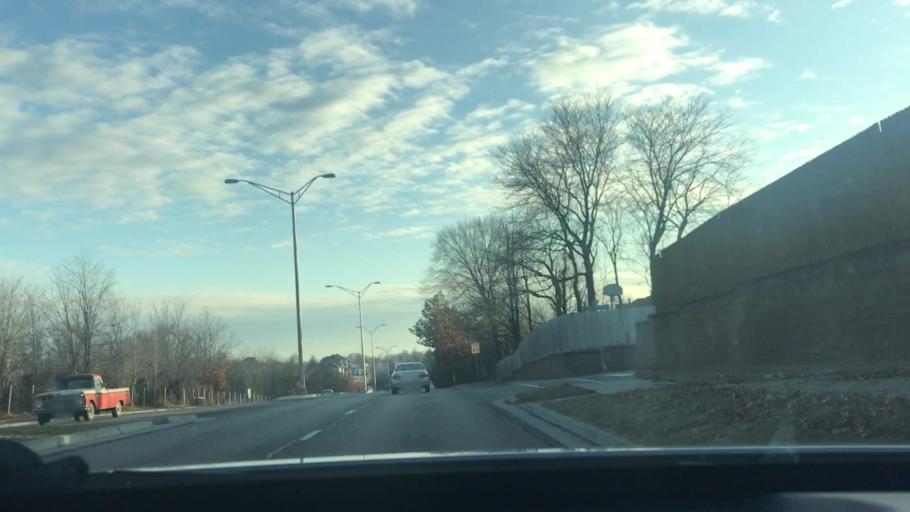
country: US
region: Missouri
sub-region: Jackson County
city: Lees Summit
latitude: 38.9415
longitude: -94.3437
